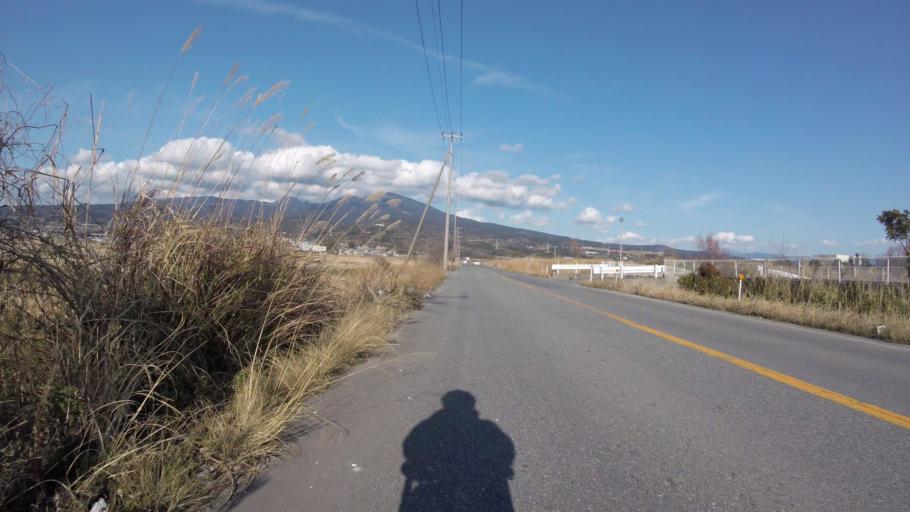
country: JP
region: Shizuoka
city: Numazu
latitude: 35.1364
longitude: 138.7827
